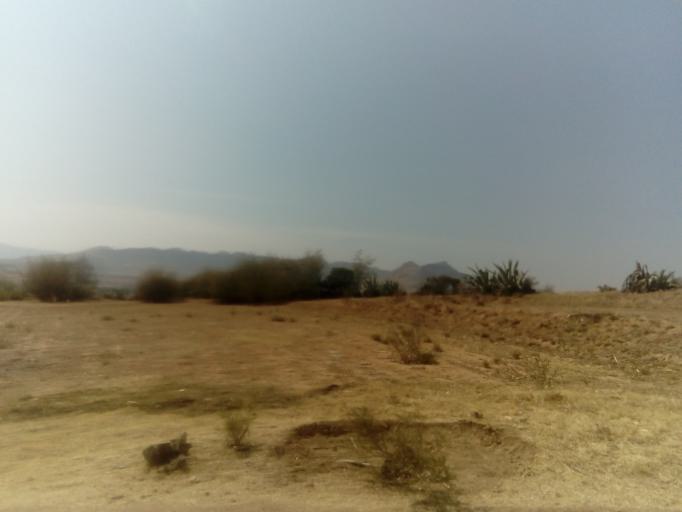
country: LS
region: Leribe
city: Leribe
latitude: -29.1336
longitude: 28.0594
